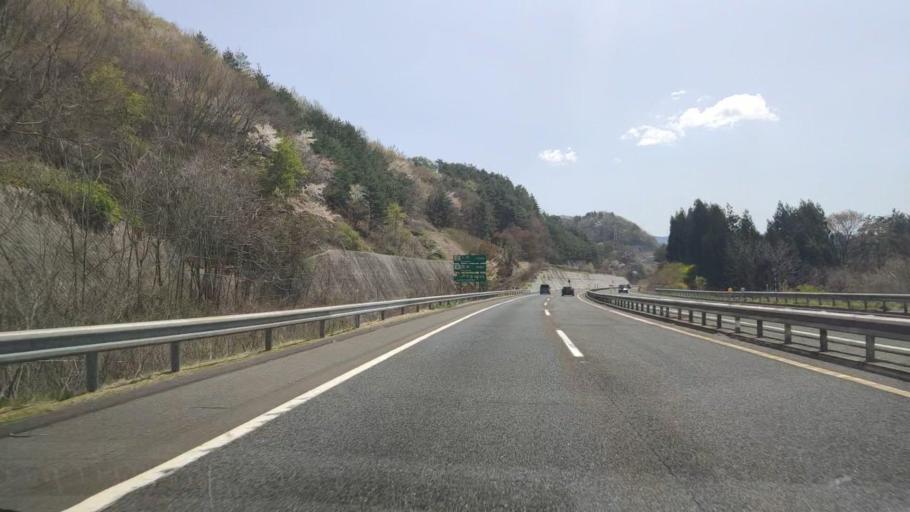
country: JP
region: Iwate
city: Ichinohe
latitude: 40.2289
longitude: 141.3211
